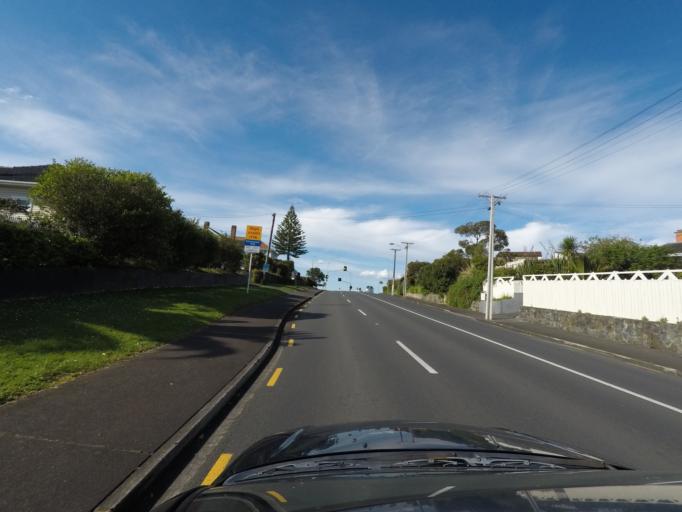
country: NZ
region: Auckland
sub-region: Auckland
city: Rosebank
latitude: -36.8974
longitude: 174.7001
